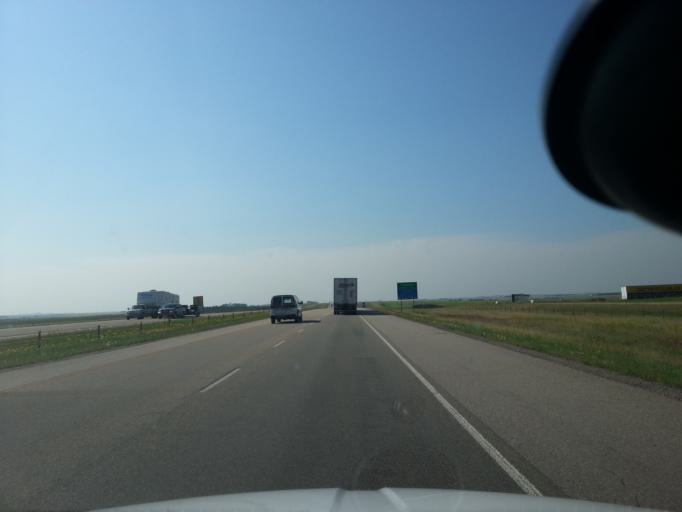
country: CA
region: Alberta
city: Carstairs
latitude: 51.5839
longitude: -114.0253
